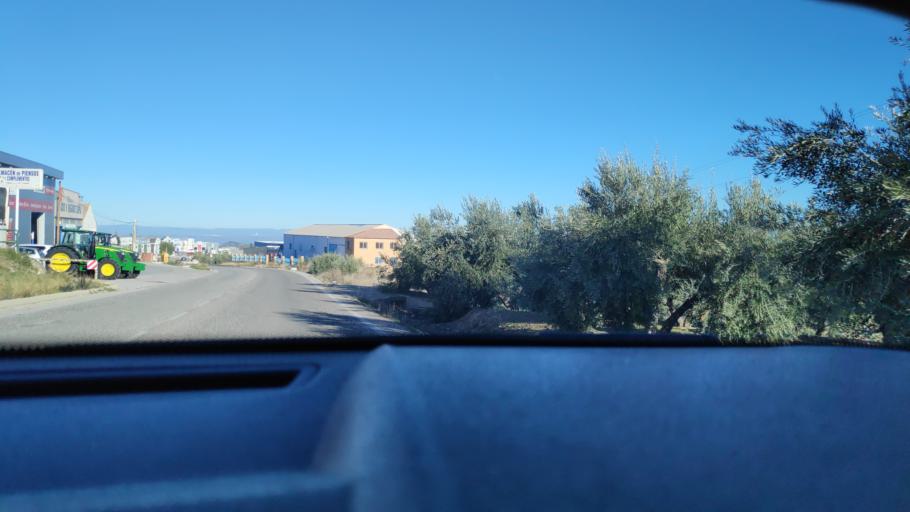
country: ES
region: Andalusia
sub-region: Provincia de Jaen
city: Mancha Real
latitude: 37.7958
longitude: -3.6076
